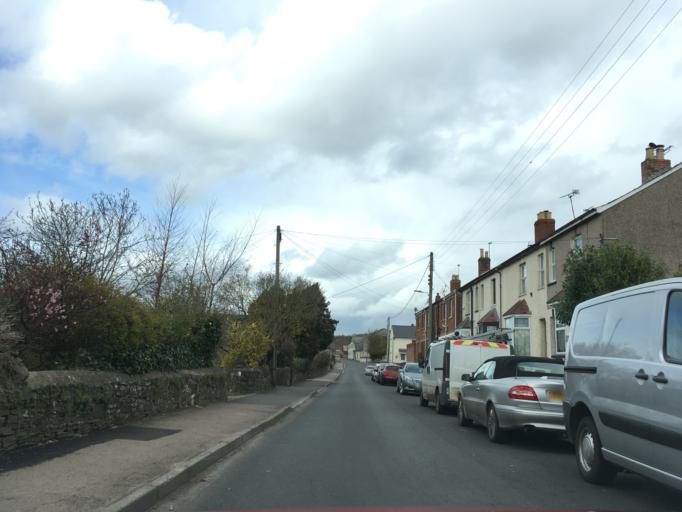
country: GB
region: England
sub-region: Gloucestershire
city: Cinderford
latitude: 51.8202
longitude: -2.5007
